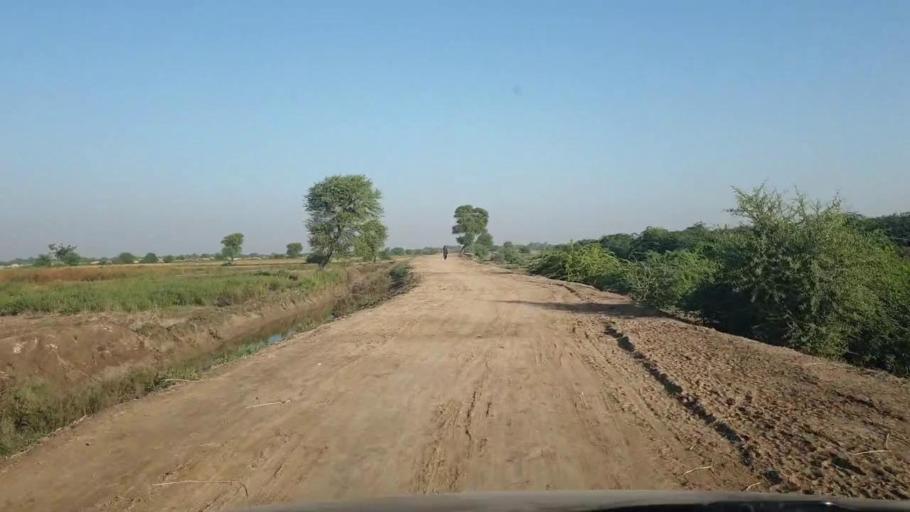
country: PK
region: Sindh
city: Badin
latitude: 24.6822
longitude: 68.8159
